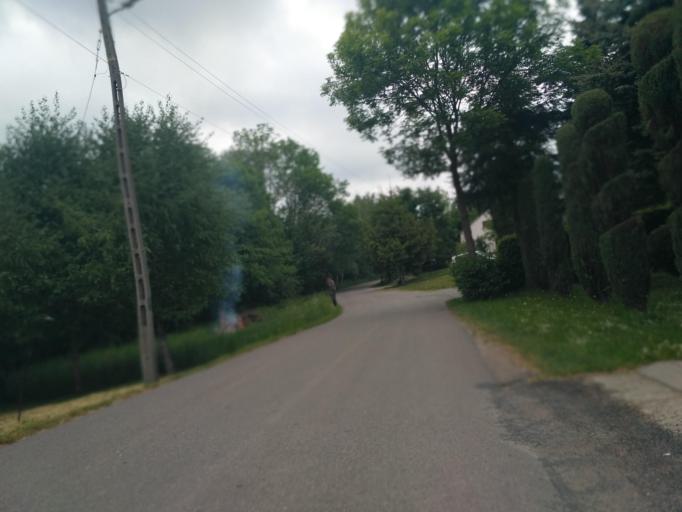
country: PL
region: Subcarpathian Voivodeship
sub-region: Powiat krosnienski
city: Chorkowka
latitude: 49.6703
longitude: 21.6967
